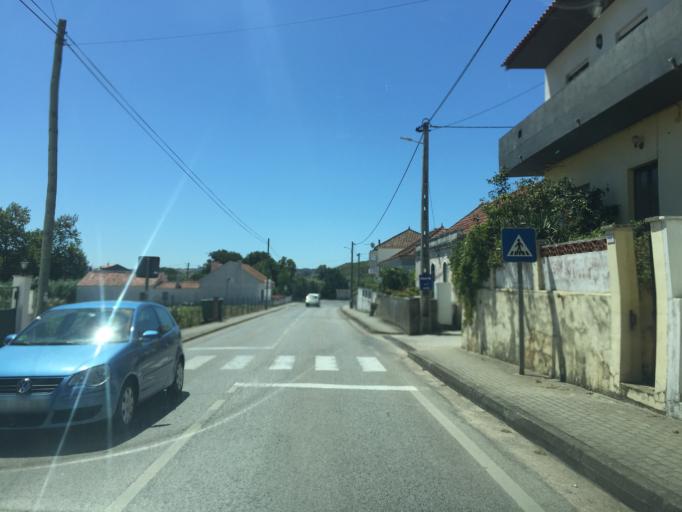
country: PT
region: Lisbon
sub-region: Torres Vedras
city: A dos Cunhados
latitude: 39.1783
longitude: -9.3226
